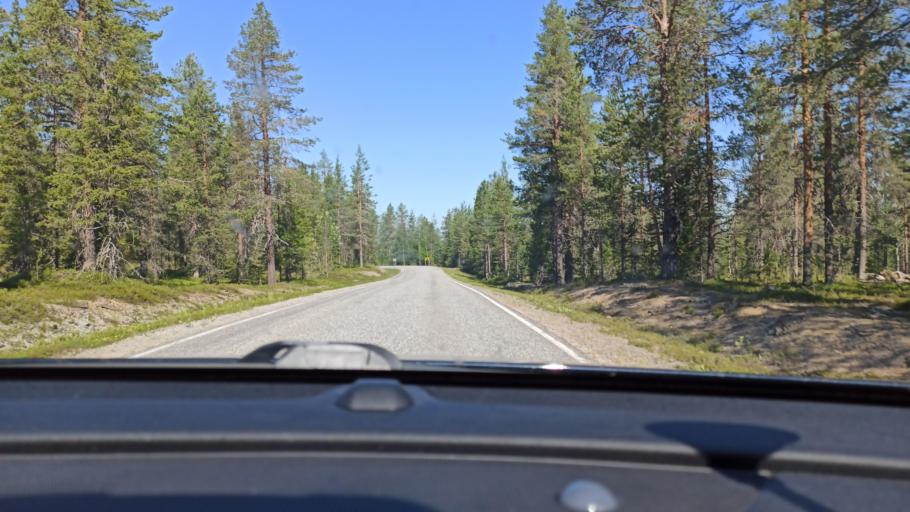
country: FI
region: Lapland
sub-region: Tunturi-Lappi
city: Kolari
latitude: 67.6809
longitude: 24.1379
